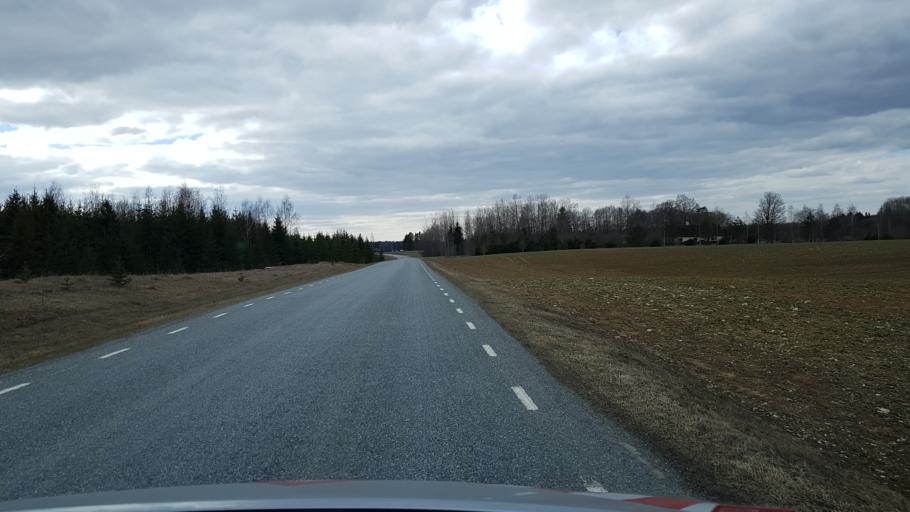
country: EE
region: Laeaene-Virumaa
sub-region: Rakvere linn
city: Rakvere
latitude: 59.2663
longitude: 26.2670
